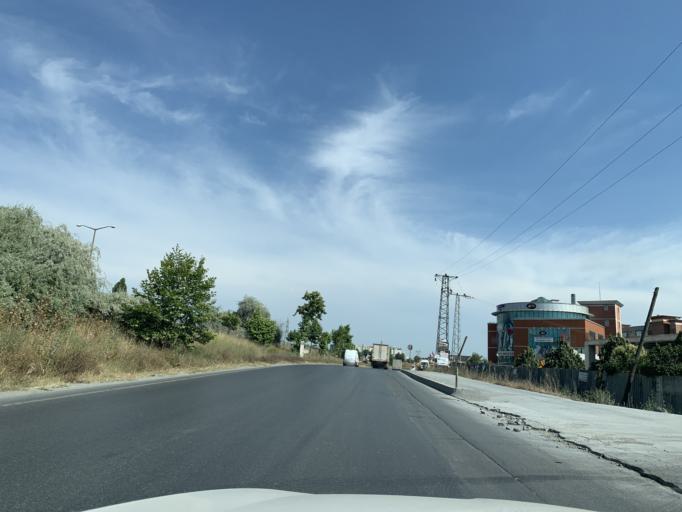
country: TR
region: Istanbul
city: Esenyurt
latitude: 41.0605
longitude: 28.6545
